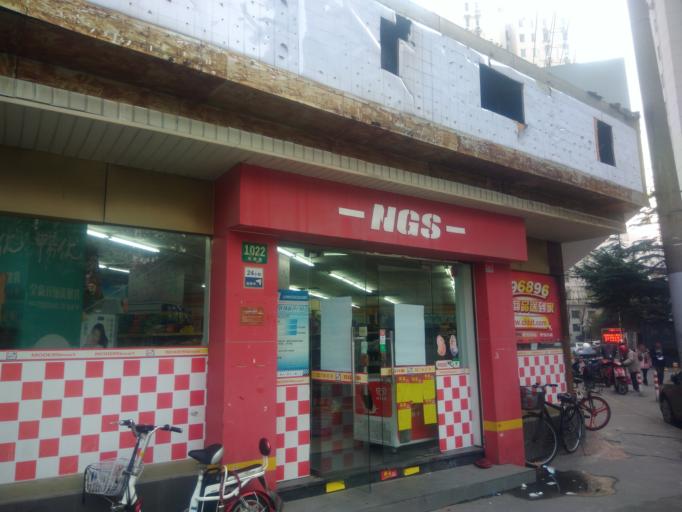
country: CN
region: Shanghai Shi
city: Changning
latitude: 31.1974
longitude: 121.4145
